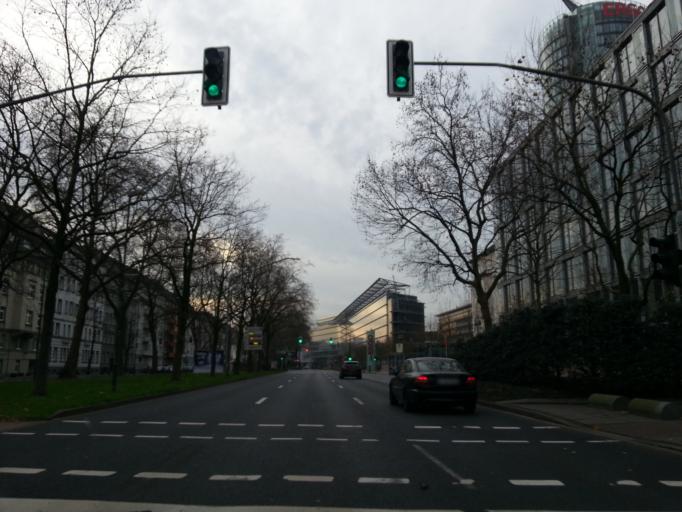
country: DE
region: North Rhine-Westphalia
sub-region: Regierungsbezirk Dusseldorf
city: Dusseldorf
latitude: 51.2386
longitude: 6.7752
